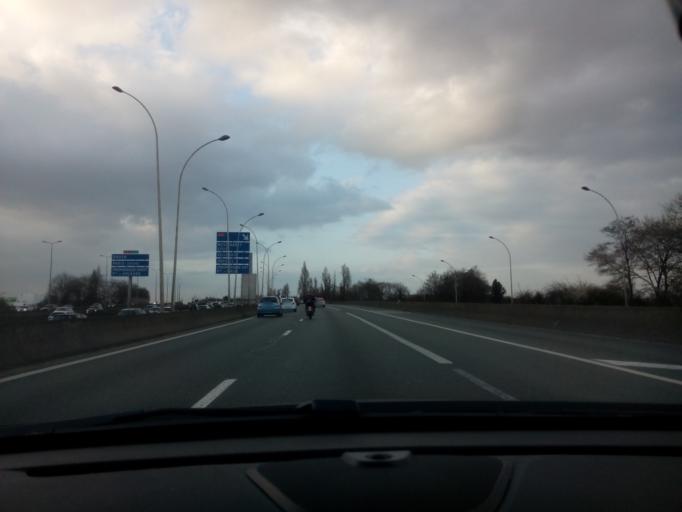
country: FR
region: Ile-de-France
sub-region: Departement du Val-de-Marne
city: L'Hay-les-Roses
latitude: 48.7817
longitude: 2.3471
